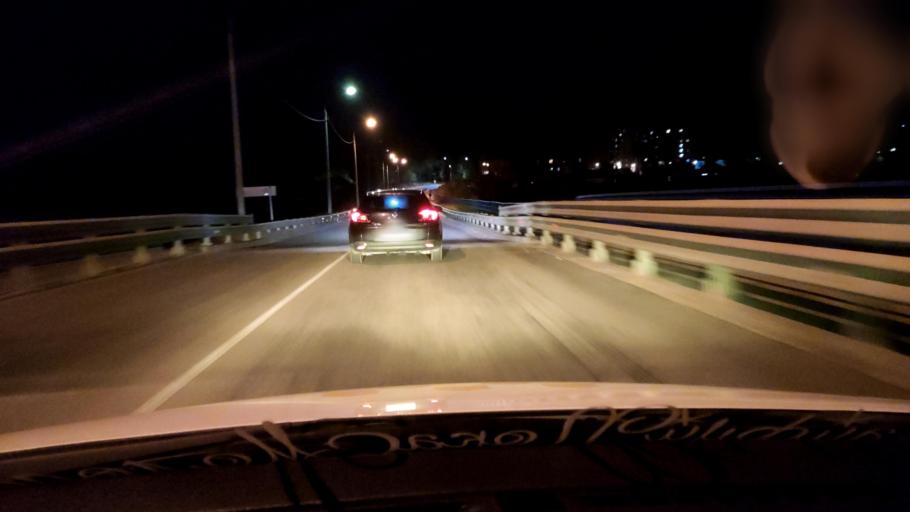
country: RU
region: Voronezj
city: Semiluki
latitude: 51.6753
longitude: 39.0321
